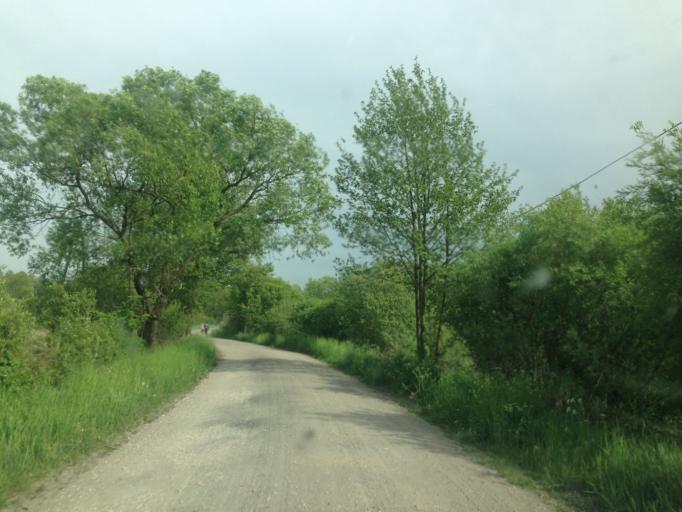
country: PL
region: Kujawsko-Pomorskie
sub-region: Powiat brodnicki
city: Brodnica
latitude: 53.2810
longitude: 19.4754
